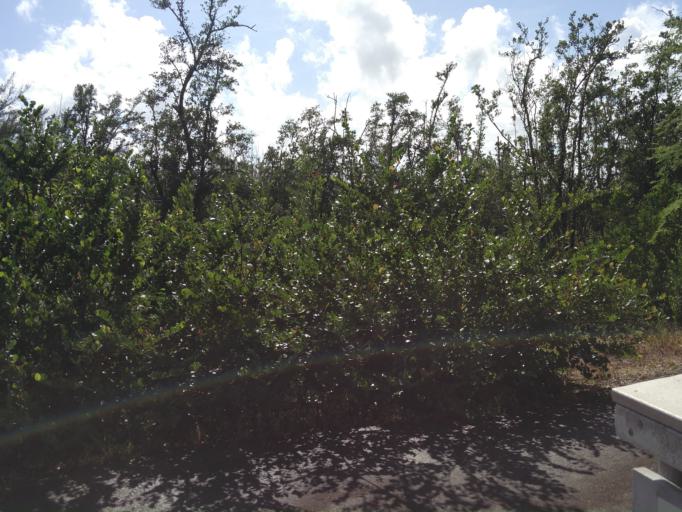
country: US
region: Florida
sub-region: Broward County
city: Dania Beach
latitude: 26.0370
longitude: -80.1195
